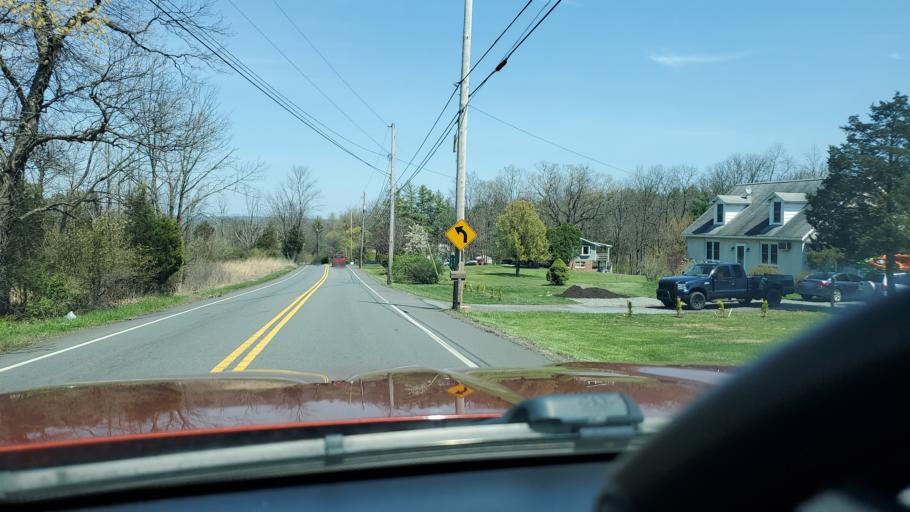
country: US
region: Pennsylvania
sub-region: Montgomery County
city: Pennsburg
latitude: 40.3568
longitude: -75.5313
